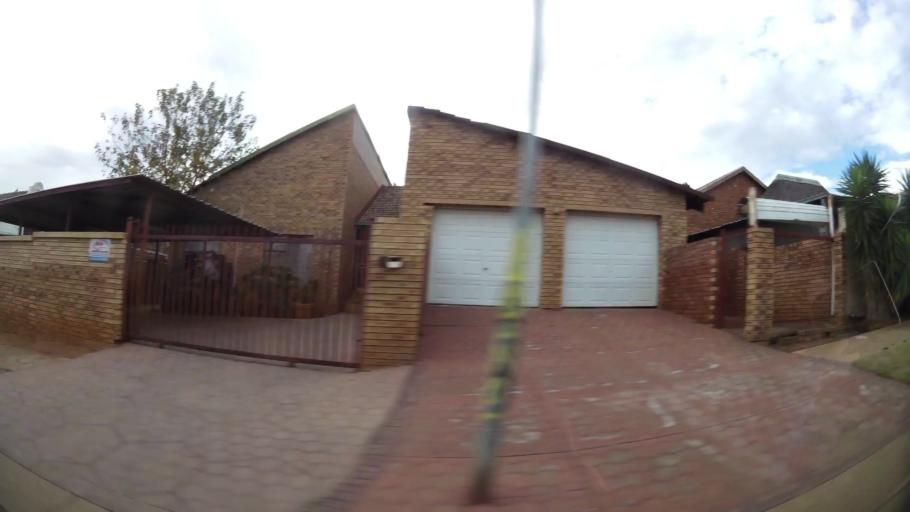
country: ZA
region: Gauteng
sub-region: City of Tshwane Metropolitan Municipality
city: Pretoria
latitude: -25.6990
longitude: 28.3090
